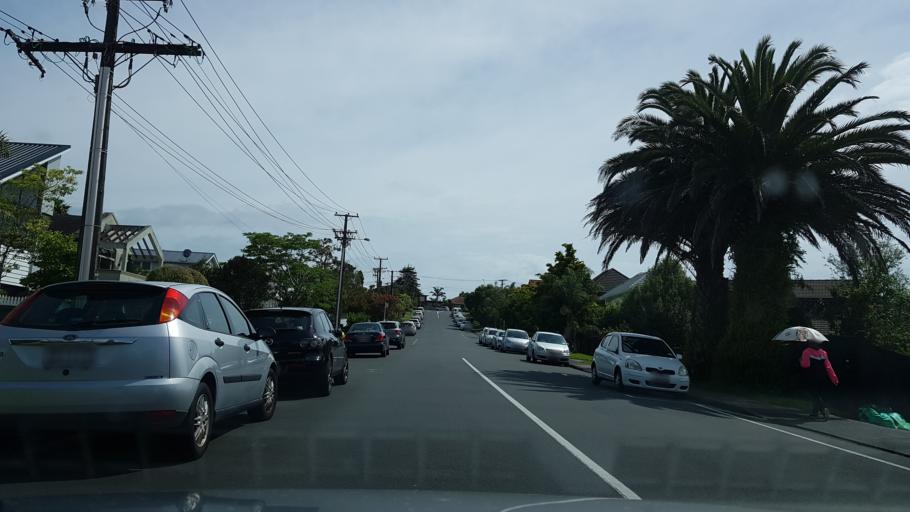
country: NZ
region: Auckland
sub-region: Auckland
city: North Shore
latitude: -36.8125
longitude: 174.7093
